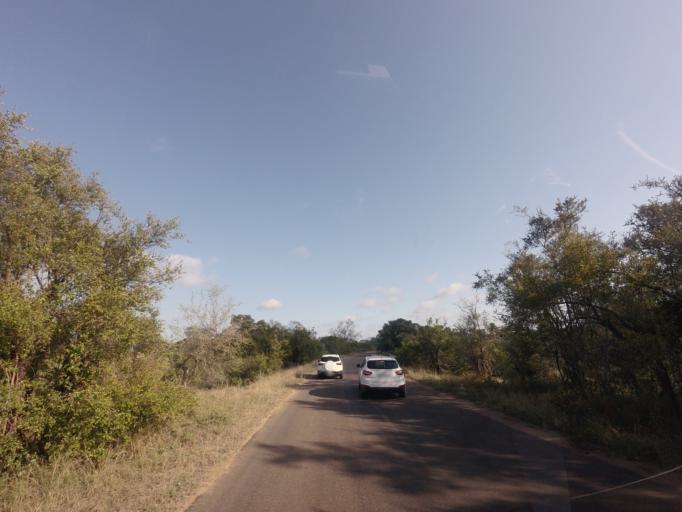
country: ZA
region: Mpumalanga
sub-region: Ehlanzeni District
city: Komatipoort
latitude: -25.2745
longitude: 31.8483
